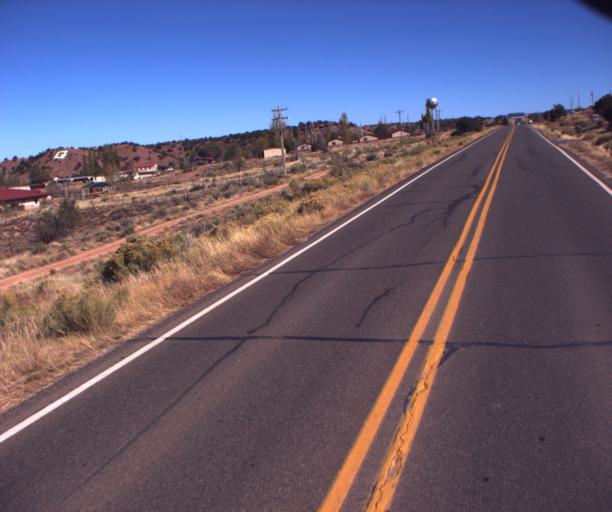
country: US
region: Arizona
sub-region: Apache County
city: Ganado
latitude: 35.7093
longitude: -109.5357
